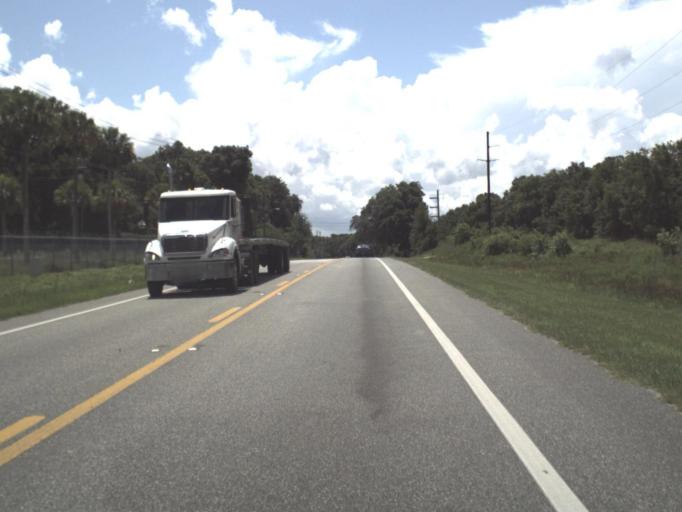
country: US
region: Florida
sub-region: Putnam County
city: Crescent City
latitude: 29.4935
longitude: -81.5896
